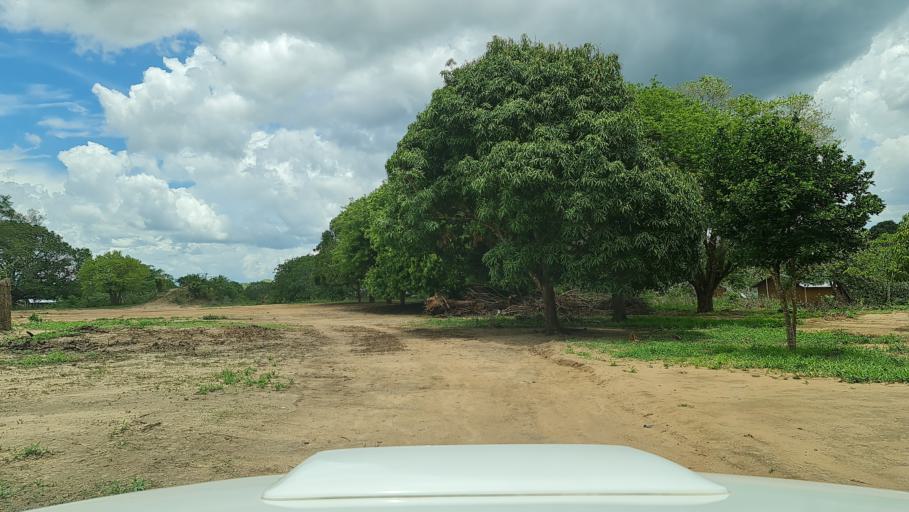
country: MZ
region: Nampula
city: Ilha de Mocambique
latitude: -15.5163
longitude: 40.2025
